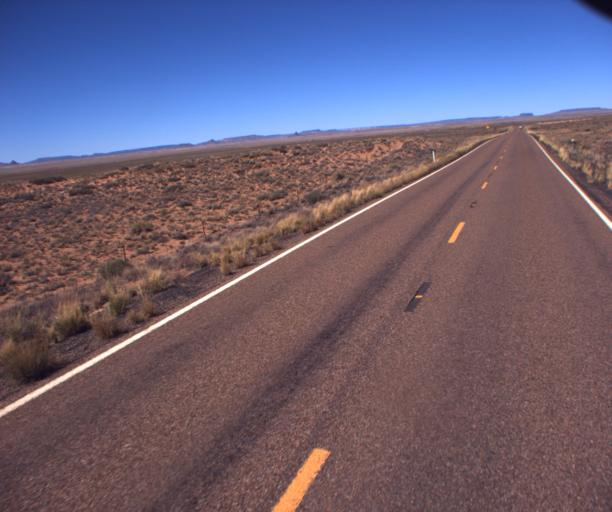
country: US
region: Arizona
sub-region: Navajo County
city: Holbrook
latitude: 35.0307
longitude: -110.0907
